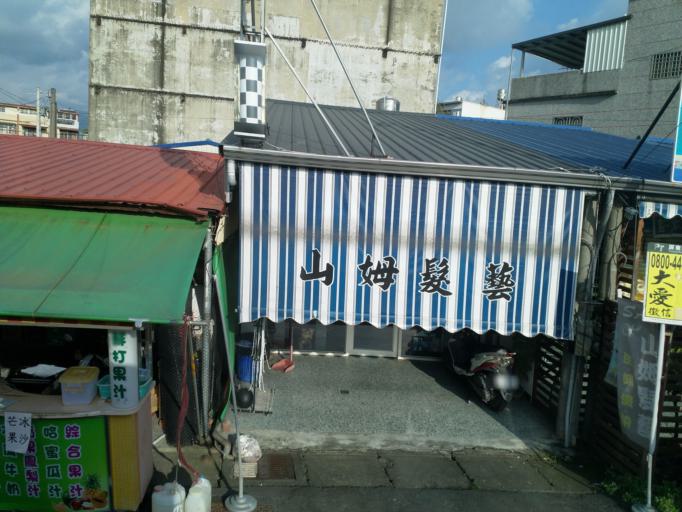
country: TW
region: Taiwan
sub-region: Pingtung
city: Pingtung
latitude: 22.8968
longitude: 120.5425
